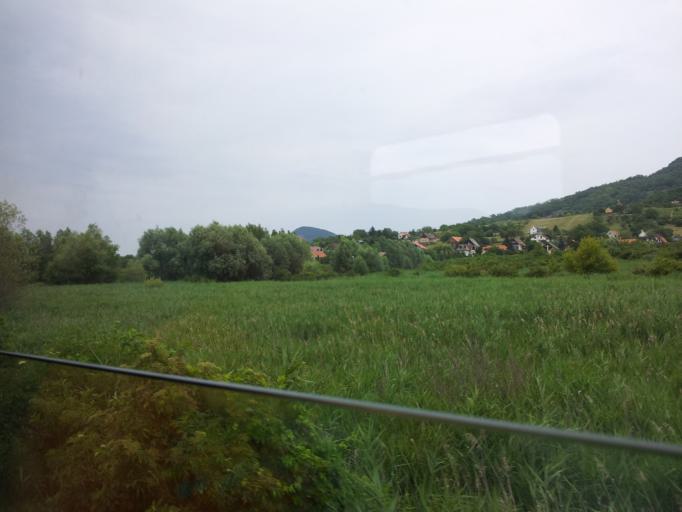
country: HU
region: Veszprem
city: Badacsonytomaj
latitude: 46.8018
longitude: 17.4690
